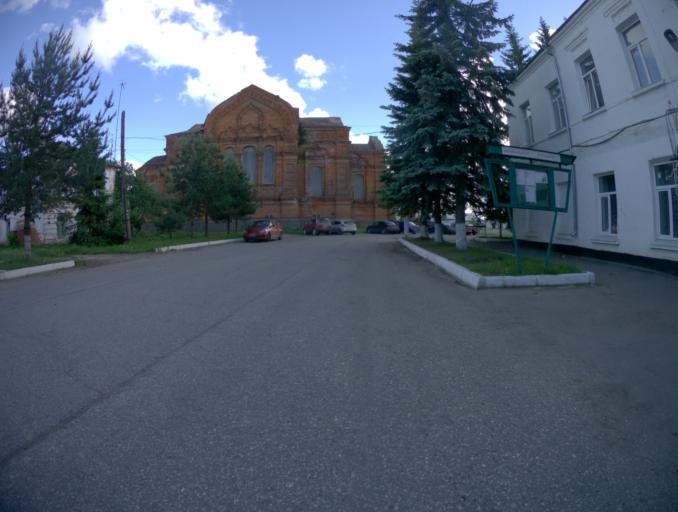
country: RU
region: Vladimir
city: Yur'yev-Pol'skiy
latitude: 56.4974
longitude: 39.6805
